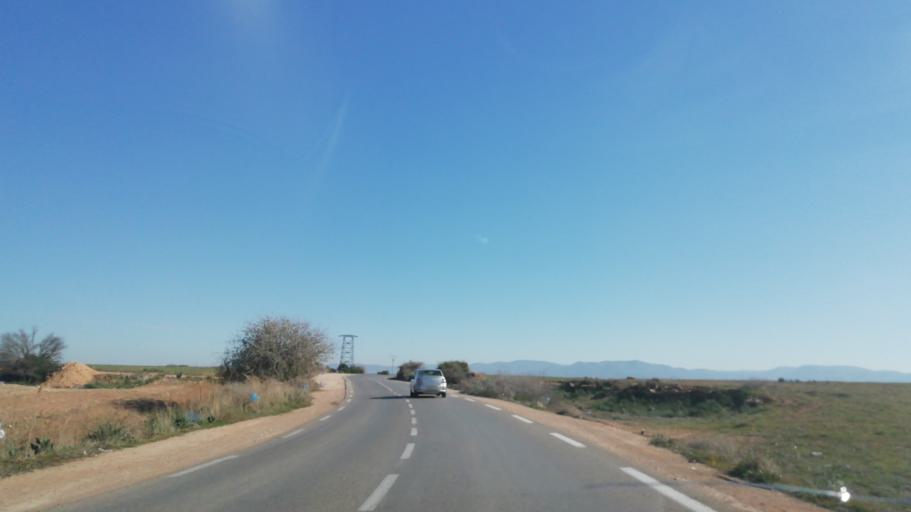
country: DZ
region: Tlemcen
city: Nedroma
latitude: 34.8328
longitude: -1.6792
